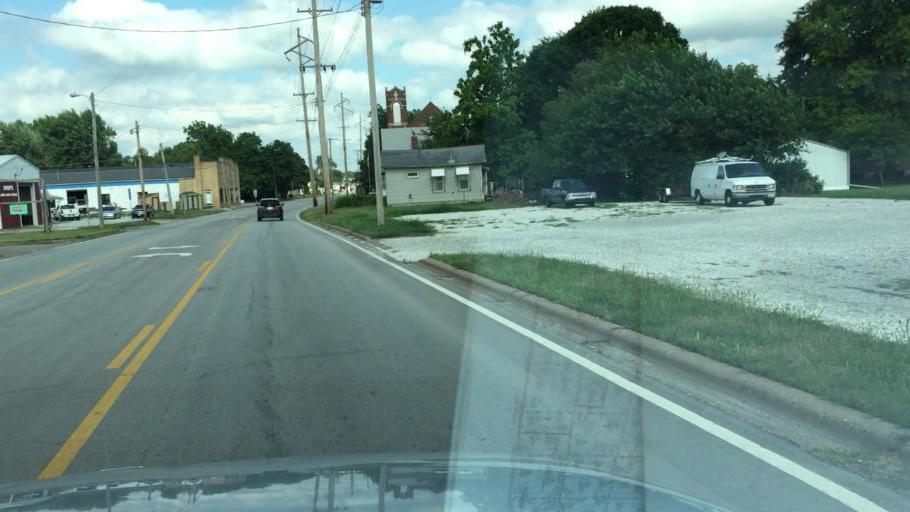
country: US
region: Illinois
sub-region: Hancock County
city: Carthage
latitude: 40.4162
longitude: -91.1417
